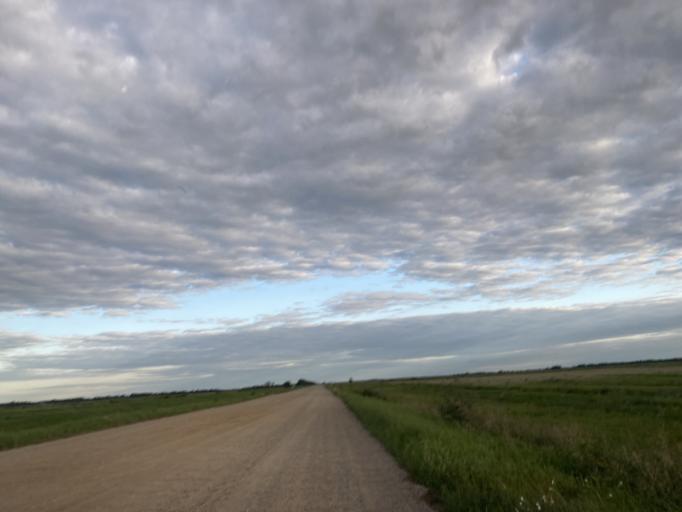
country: BY
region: Brest
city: Tsyelyakhany
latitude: 52.4575
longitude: 25.5713
